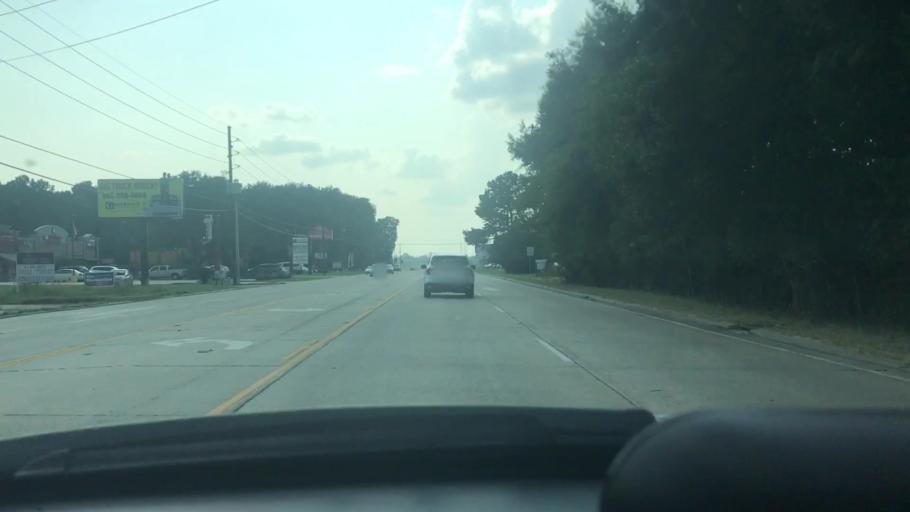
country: US
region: Louisiana
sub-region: Tangipahoa Parish
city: Natalbany
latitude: 30.5192
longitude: -90.4932
